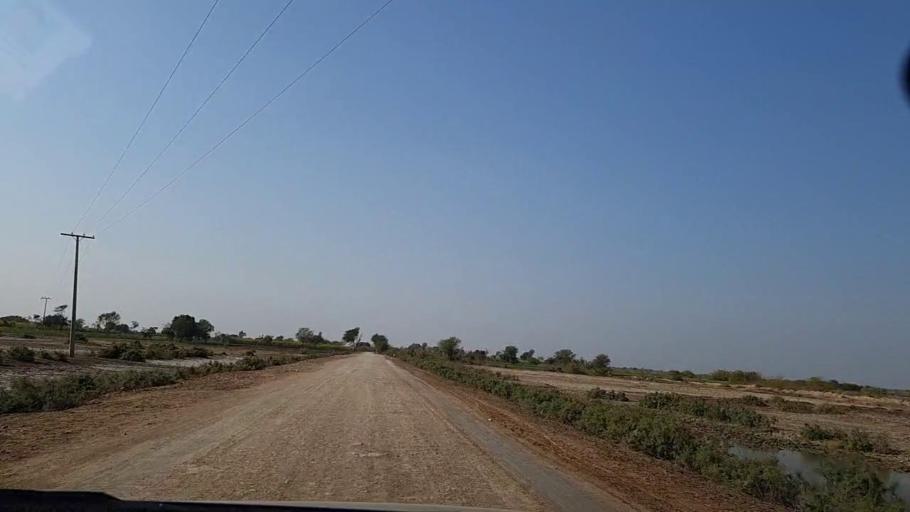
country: PK
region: Sindh
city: Digri
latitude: 25.1897
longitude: 68.9982
